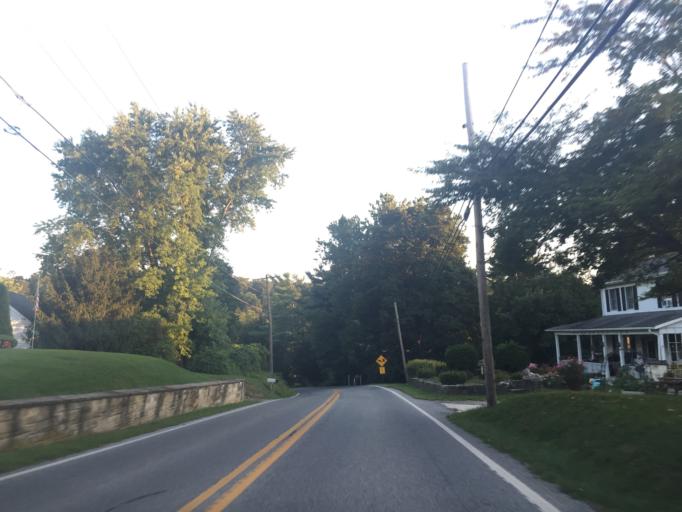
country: US
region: Pennsylvania
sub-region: York County
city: Susquehanna Trails
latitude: 39.7318
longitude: -76.3229
